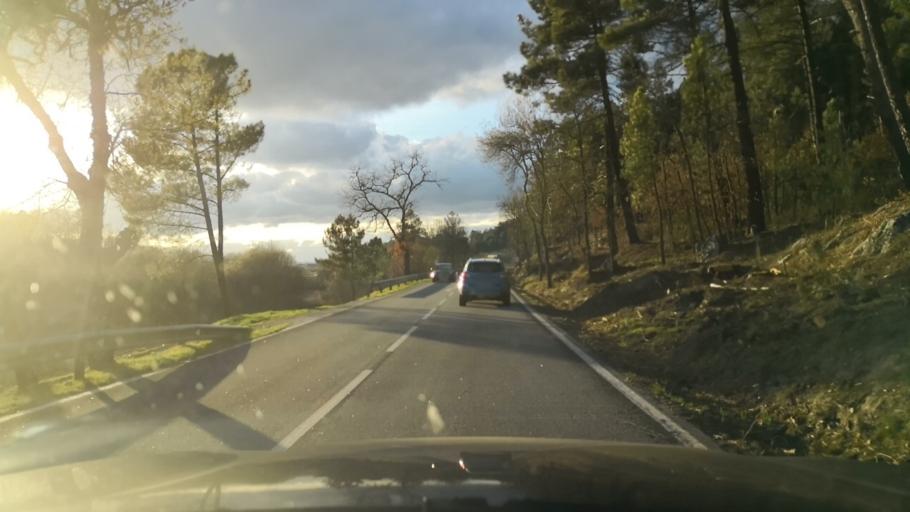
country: PT
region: Braganca
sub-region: Carrazeda de Ansiaes
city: Carrazeda de Anciaes
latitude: 41.2300
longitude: -7.3345
